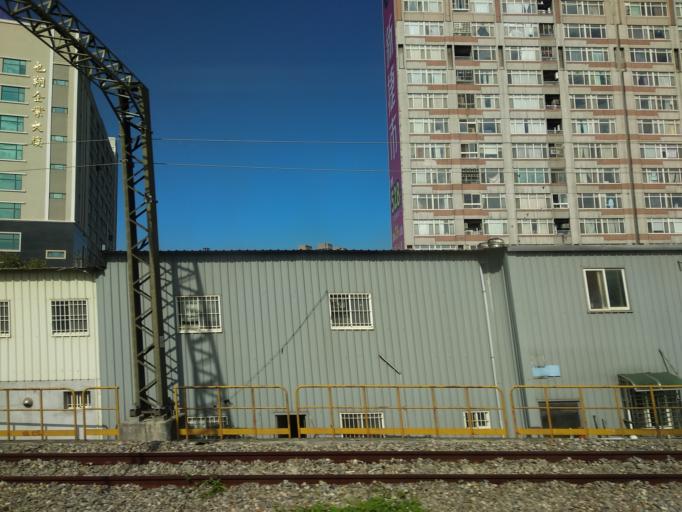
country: TW
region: Taiwan
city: Taoyuan City
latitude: 24.9804
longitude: 121.2751
